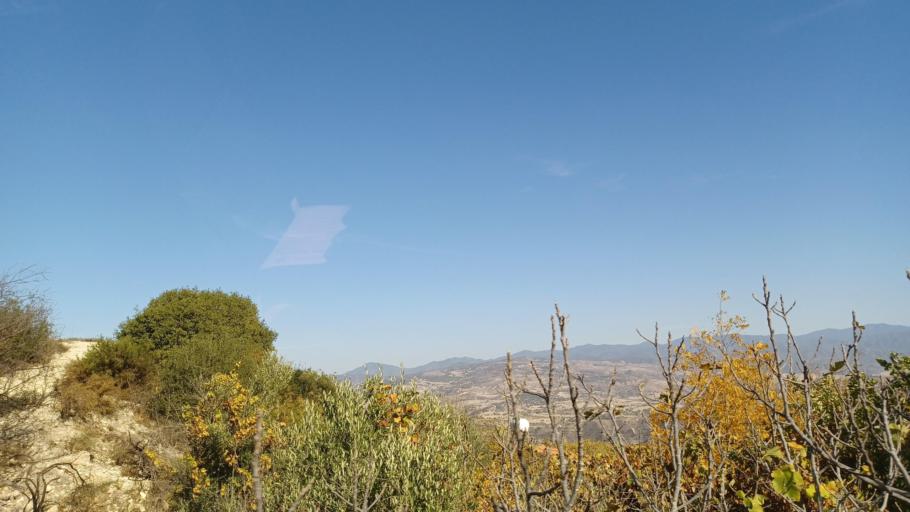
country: CY
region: Pafos
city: Pegeia
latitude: 34.9336
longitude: 32.4482
